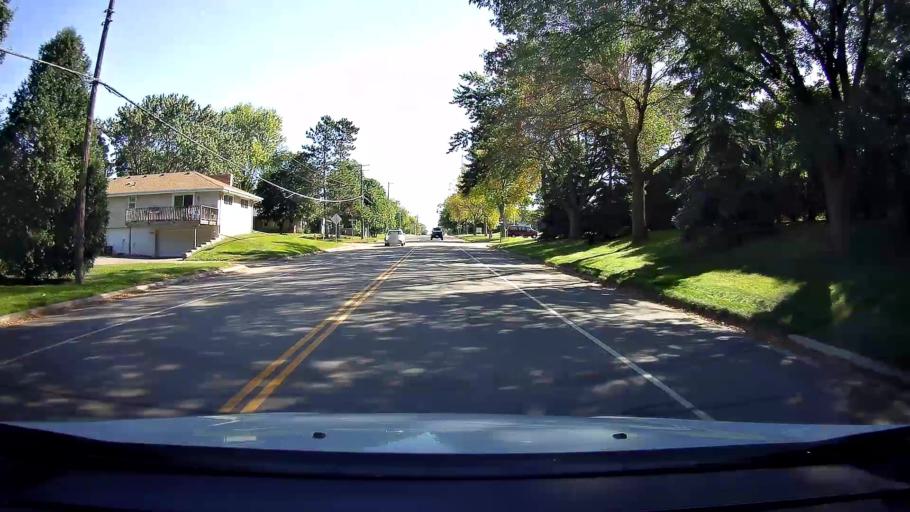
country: US
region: Minnesota
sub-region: Ramsey County
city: Roseville
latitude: 45.0227
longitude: -93.1513
